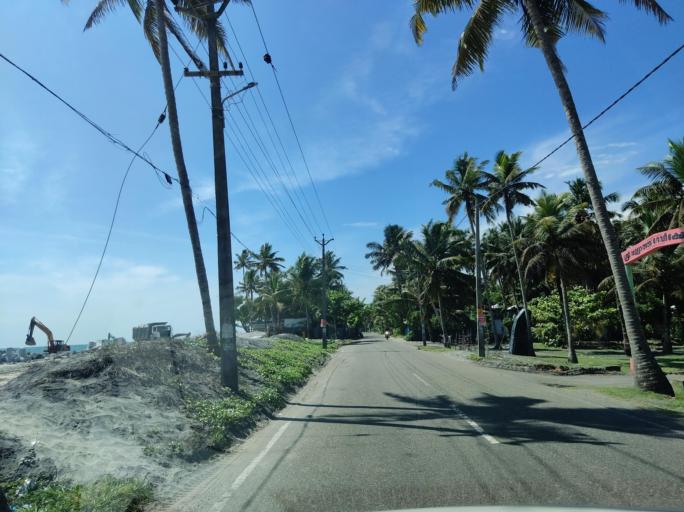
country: IN
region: Kerala
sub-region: Alappuzha
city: Kayankulam
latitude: 9.1931
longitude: 76.4376
